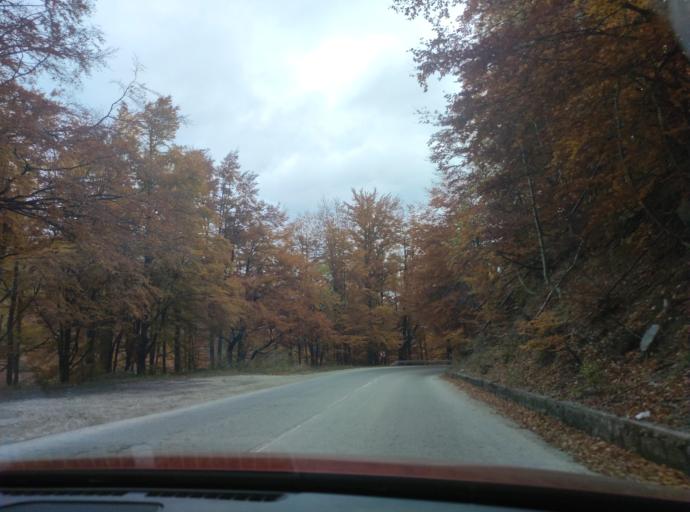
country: BG
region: Montana
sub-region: Obshtina Berkovitsa
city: Berkovitsa
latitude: 43.1296
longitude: 23.1413
